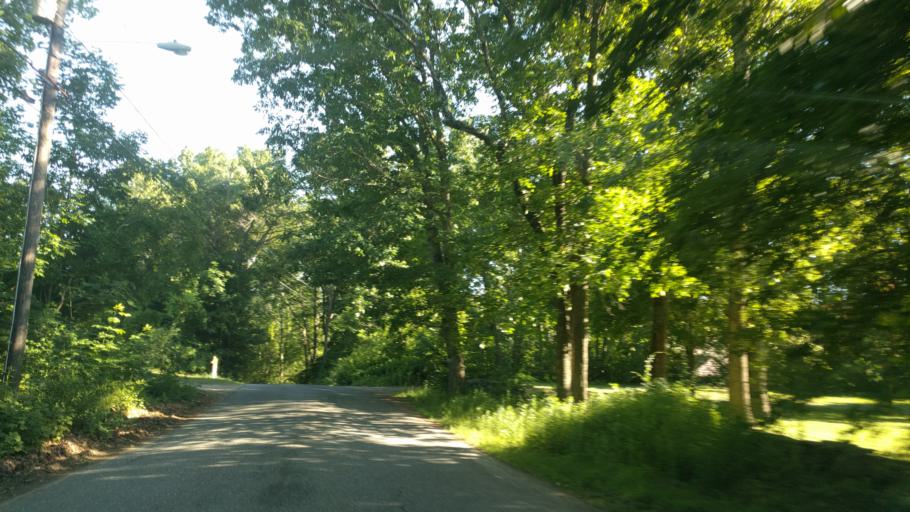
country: US
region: Massachusetts
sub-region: Worcester County
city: Oxford
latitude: 42.1378
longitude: -71.8355
